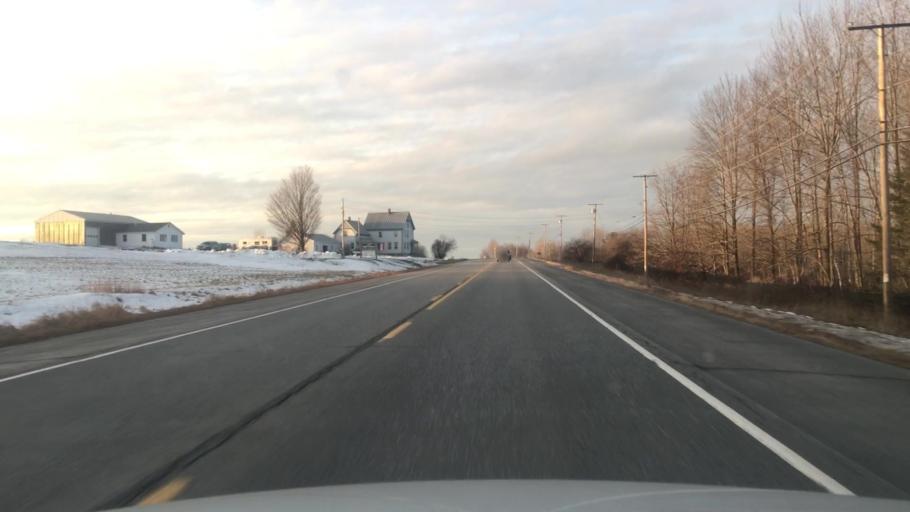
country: US
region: Maine
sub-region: Somerset County
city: Fairfield
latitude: 44.6387
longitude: -69.6013
